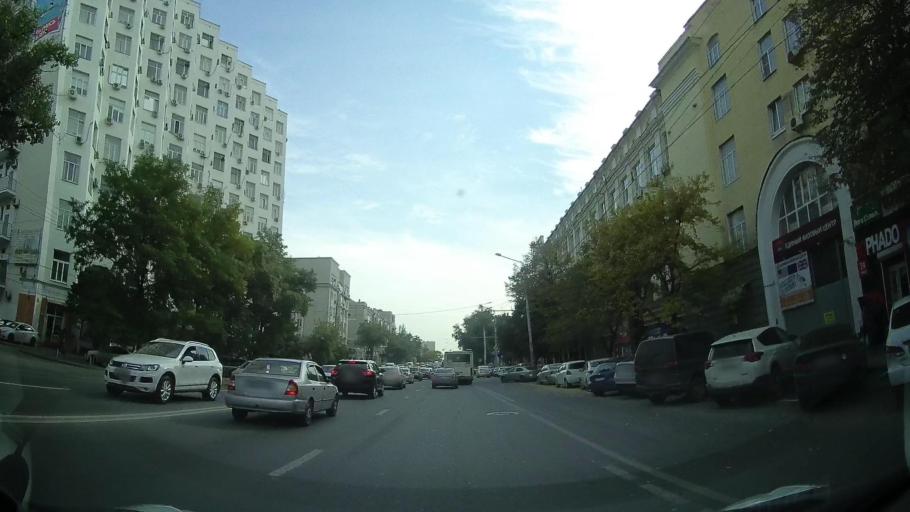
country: RU
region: Rostov
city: Rostov-na-Donu
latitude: 47.2333
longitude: 39.7017
